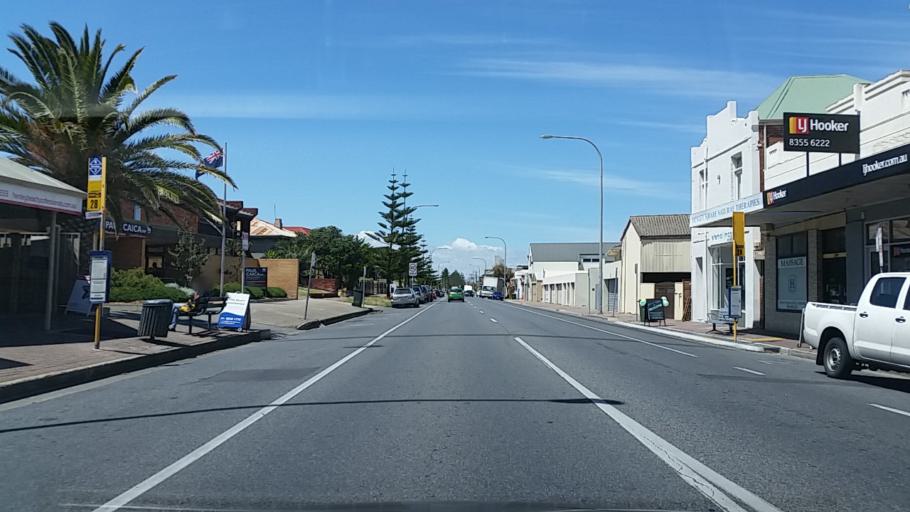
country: AU
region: South Australia
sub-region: Charles Sturt
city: Henley Beach
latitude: -34.9200
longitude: 138.4945
